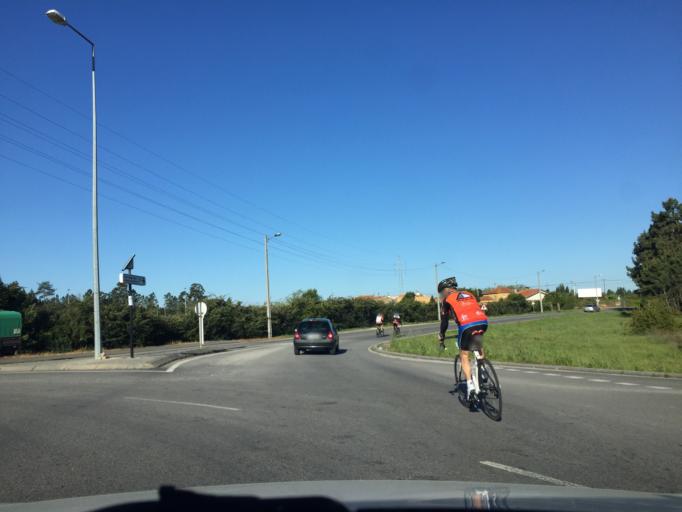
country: PT
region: Aveiro
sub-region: Anadia
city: Arcos
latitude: 40.4448
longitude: -8.4583
